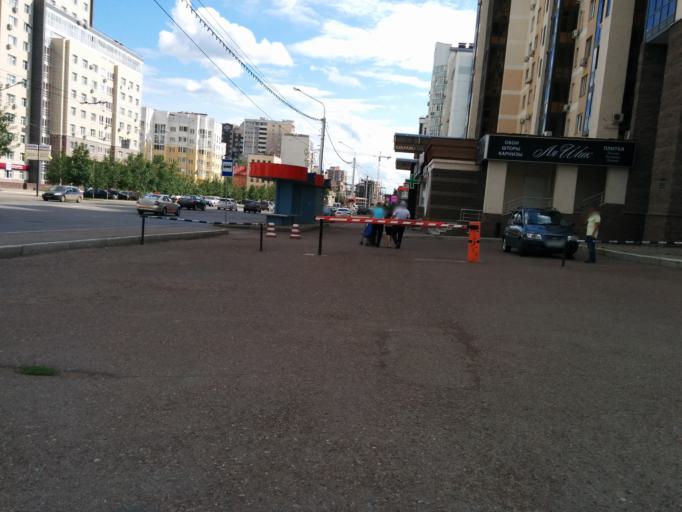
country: RU
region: Bashkortostan
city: Ufa
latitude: 54.7299
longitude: 55.9554
